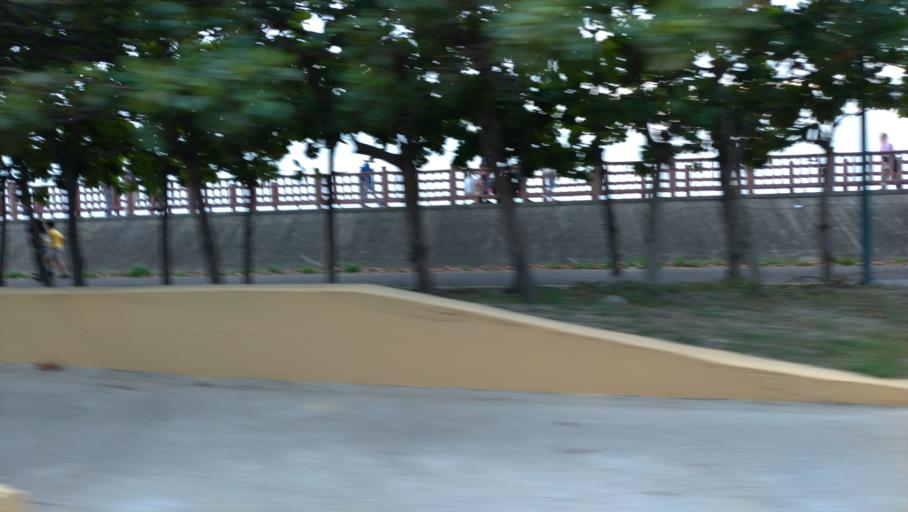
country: TW
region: Taiwan
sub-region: Hsinchu
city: Hsinchu
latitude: 24.7807
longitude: 120.9149
